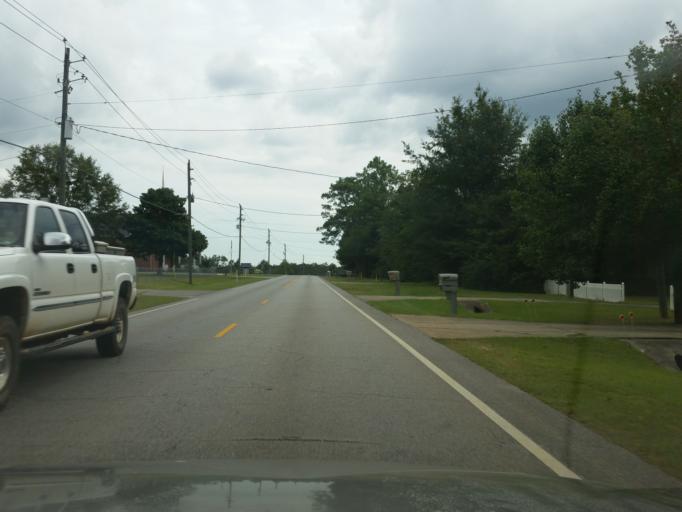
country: US
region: Florida
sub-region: Escambia County
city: Molino
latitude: 30.7138
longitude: -87.3370
